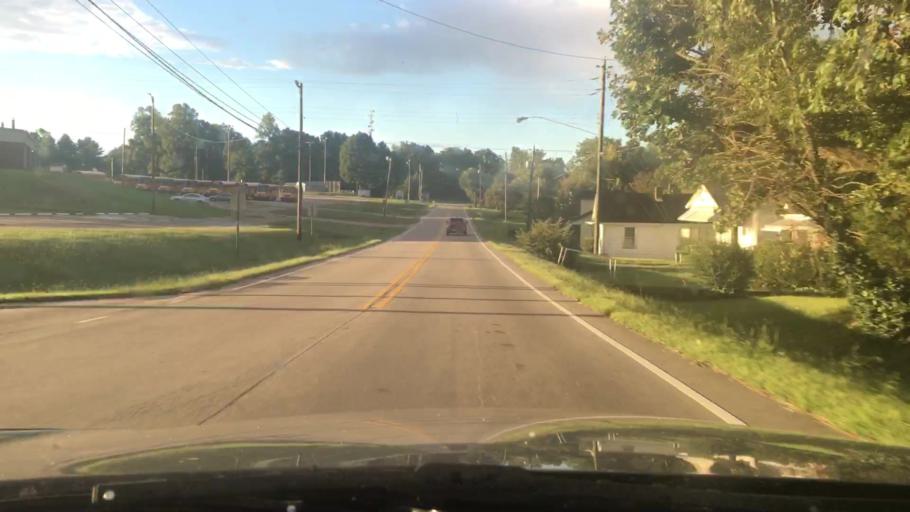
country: US
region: North Carolina
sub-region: Caswell County
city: Yanceyville
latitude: 36.4038
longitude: -79.3293
